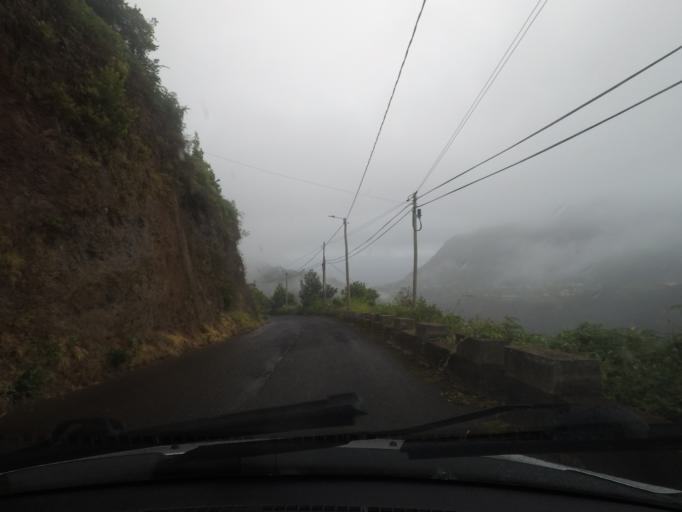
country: PT
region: Madeira
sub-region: Santana
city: Santana
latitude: 32.7790
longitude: -16.8628
